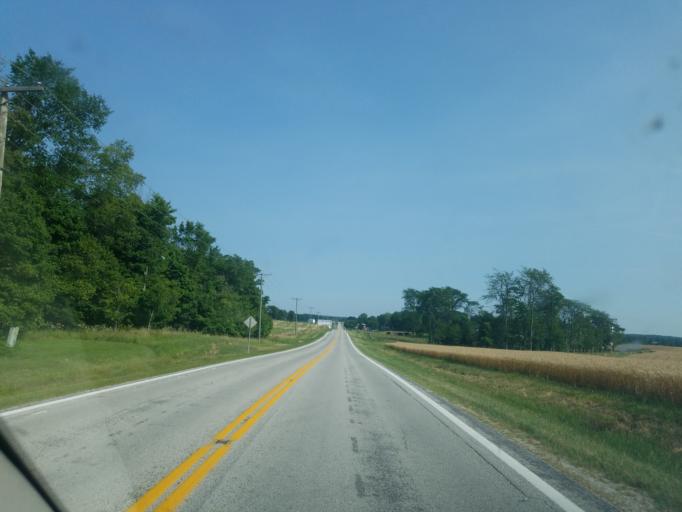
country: US
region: Ohio
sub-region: Wyandot County
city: Carey
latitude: 41.0130
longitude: -83.2841
